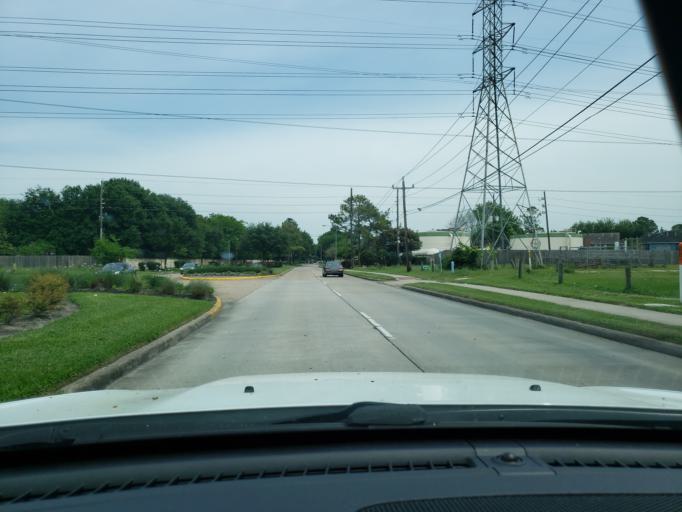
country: US
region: Texas
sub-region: Harris County
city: Jersey Village
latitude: 29.9095
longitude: -95.5785
